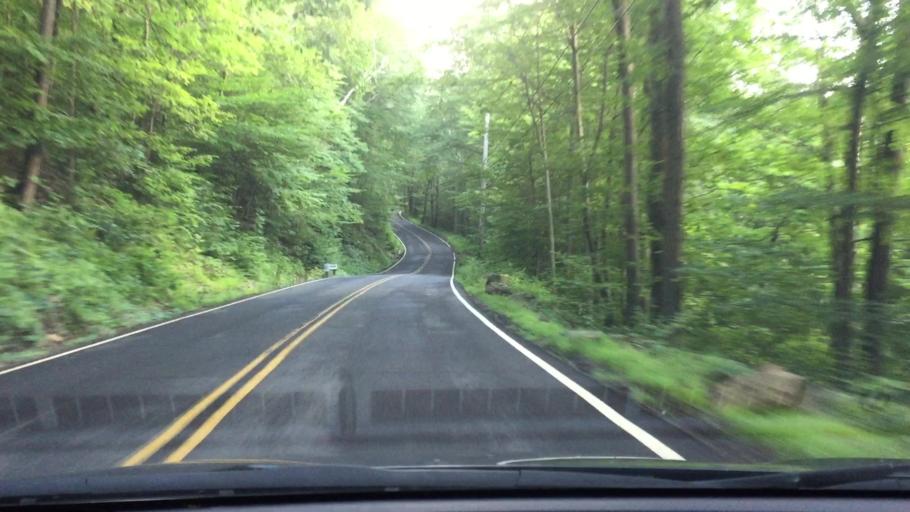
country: US
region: Massachusetts
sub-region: Hampshire County
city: Southampton
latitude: 42.1984
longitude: -72.8464
